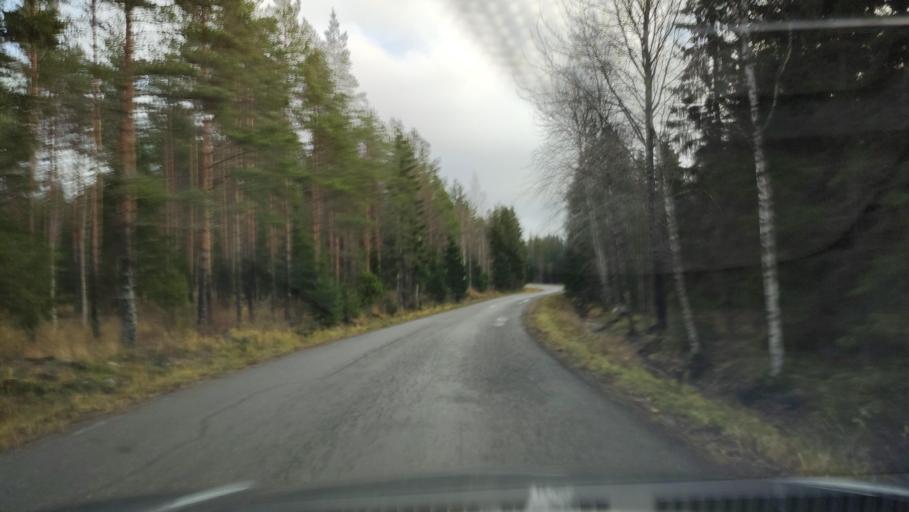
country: FI
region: Ostrobothnia
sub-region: Sydosterbotten
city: Kristinestad
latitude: 62.1536
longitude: 21.5293
